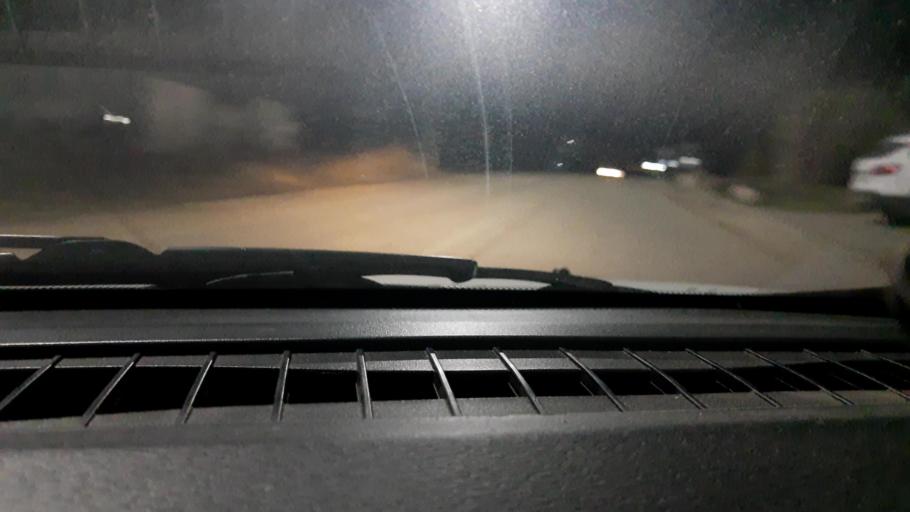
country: RU
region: Nizjnij Novgorod
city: Afonino
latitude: 56.2745
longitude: 44.0463
